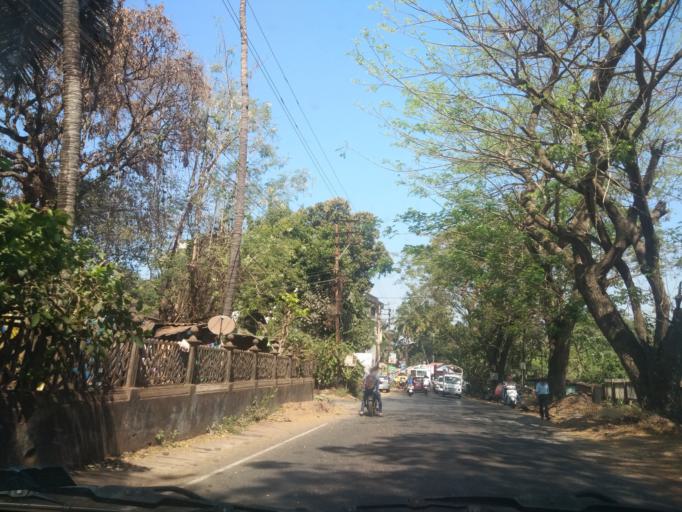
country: IN
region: Goa
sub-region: North Goa
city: Mapuca
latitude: 15.6009
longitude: 73.8157
